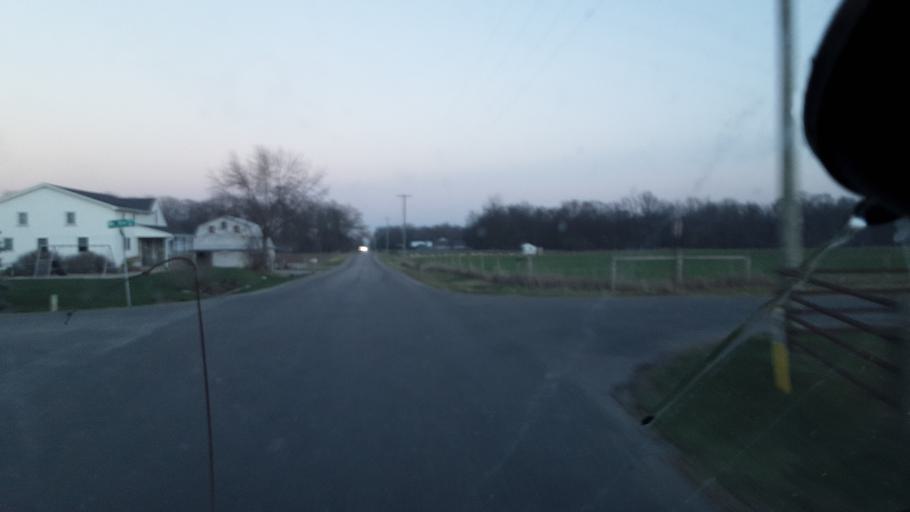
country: US
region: Indiana
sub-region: Allen County
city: Harlan
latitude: 41.2396
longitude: -84.9237
